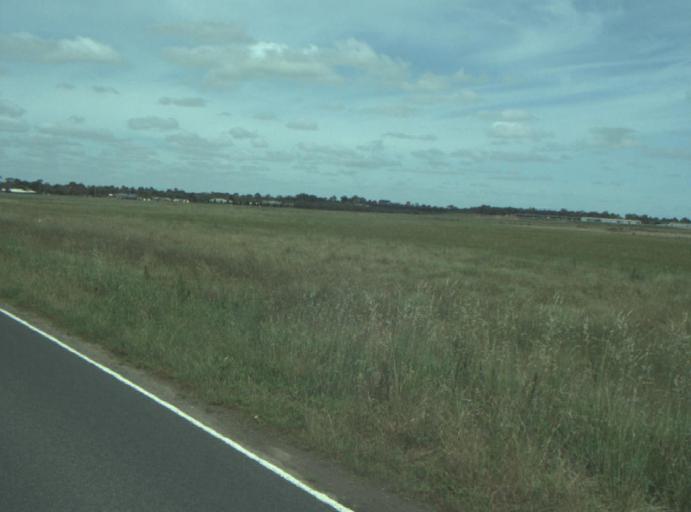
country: AU
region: Victoria
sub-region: Greater Geelong
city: Lara
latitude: -38.0110
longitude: 144.4573
